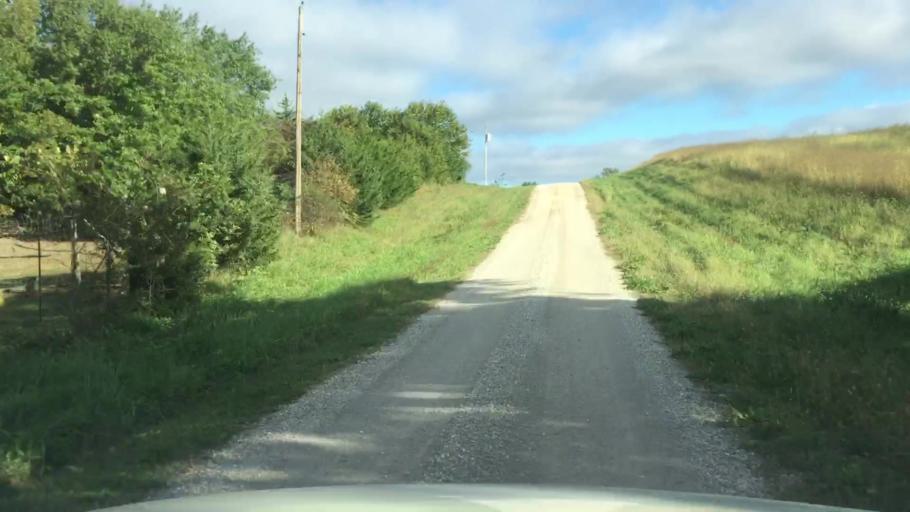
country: US
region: Missouri
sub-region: Howard County
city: New Franklin
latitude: 39.0952
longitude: -92.7795
